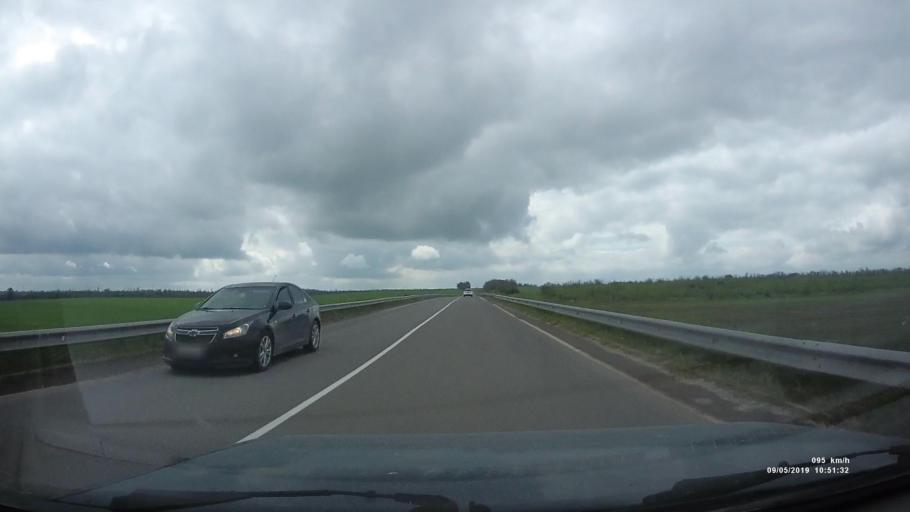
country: RU
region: Rostov
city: Peshkovo
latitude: 46.9134
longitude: 39.3551
